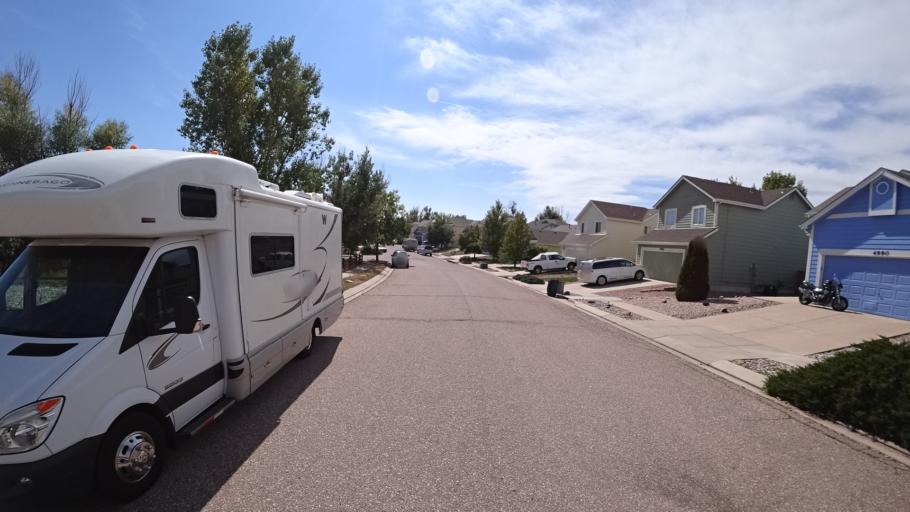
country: US
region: Colorado
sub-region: El Paso County
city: Cimarron Hills
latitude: 38.9027
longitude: -104.7122
